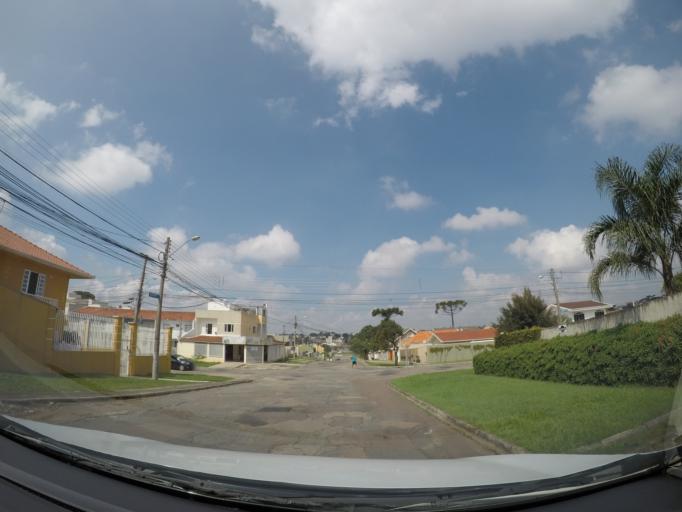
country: BR
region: Parana
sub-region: Sao Jose Dos Pinhais
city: Sao Jose dos Pinhais
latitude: -25.4929
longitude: -49.2587
